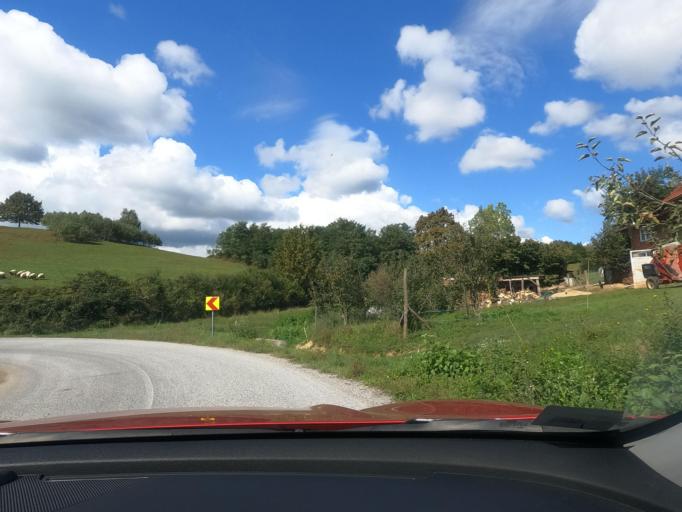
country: BA
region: Federation of Bosnia and Herzegovina
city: Velika Kladusa
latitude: 45.2143
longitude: 15.8221
